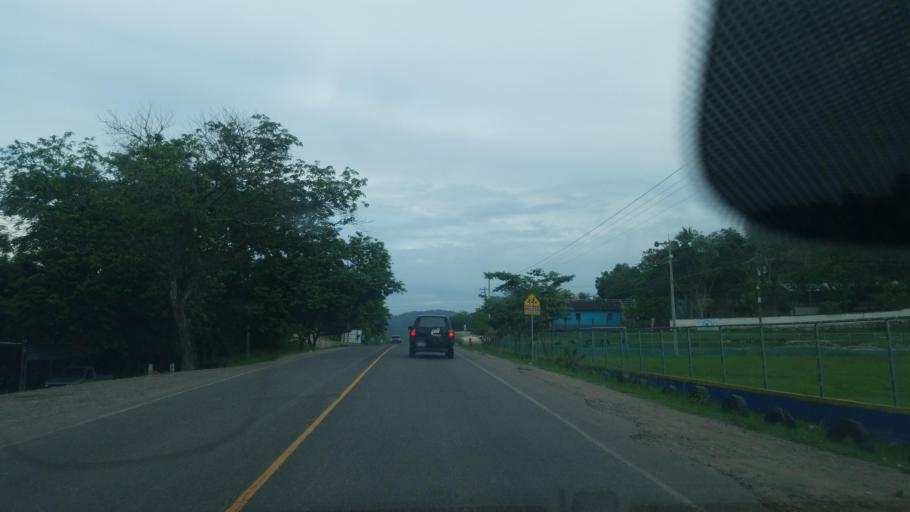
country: HN
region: Santa Barbara
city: Santa Barbara
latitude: 14.8991
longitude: -88.2525
